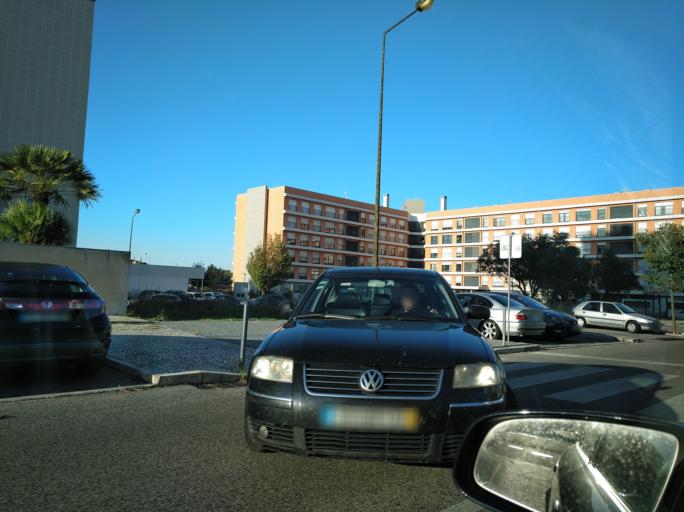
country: PT
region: Lisbon
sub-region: Odivelas
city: Olival do Basto
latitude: 38.7708
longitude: -9.1701
